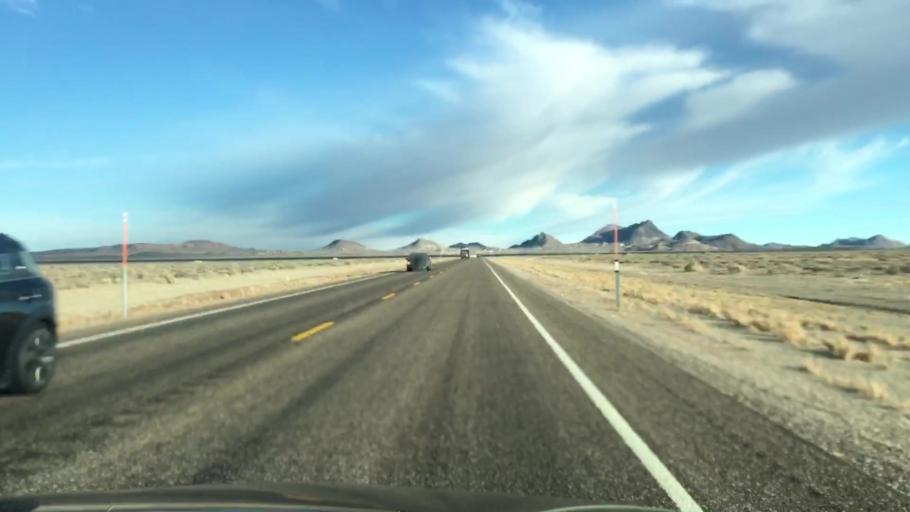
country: US
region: Nevada
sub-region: Nye County
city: Tonopah
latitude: 38.1020
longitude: -117.3346
